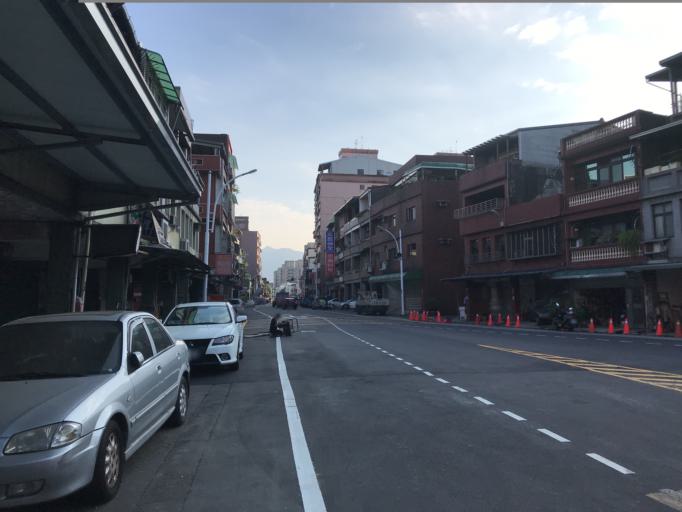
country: TW
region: Taiwan
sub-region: Taoyuan
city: Taoyuan
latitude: 24.9267
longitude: 121.3684
